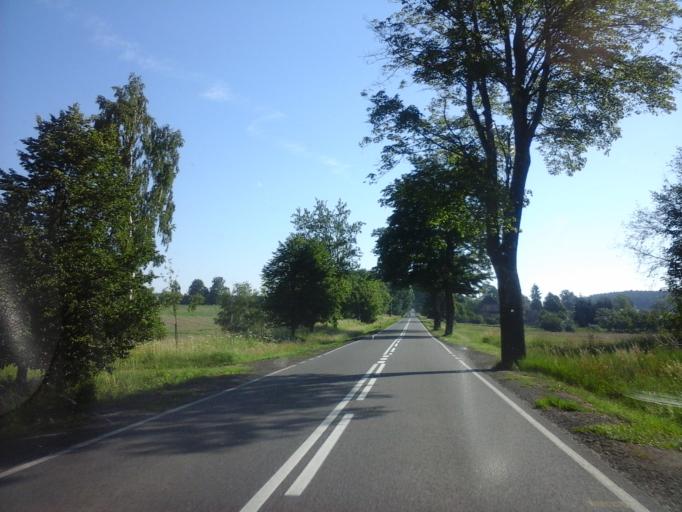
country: PL
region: West Pomeranian Voivodeship
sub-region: Powiat drawski
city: Drawsko Pomorskie
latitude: 53.5085
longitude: 15.7595
